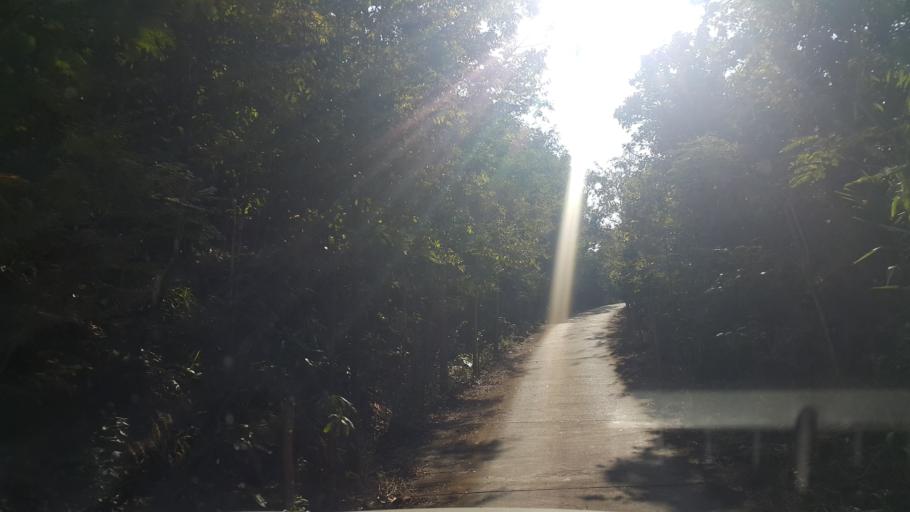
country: TH
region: Lamphun
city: Ban Thi
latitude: 18.5808
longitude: 99.1308
